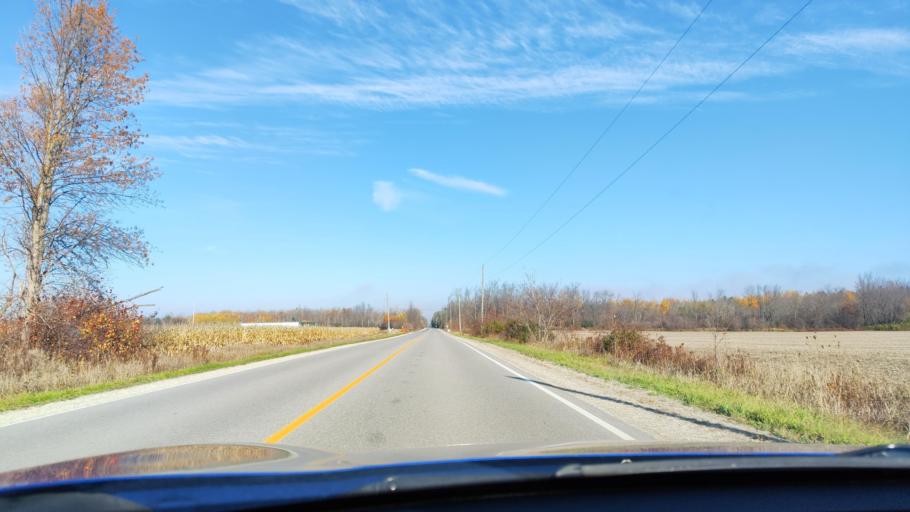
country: CA
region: Ontario
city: Wasaga Beach
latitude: 44.4006
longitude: -80.0579
